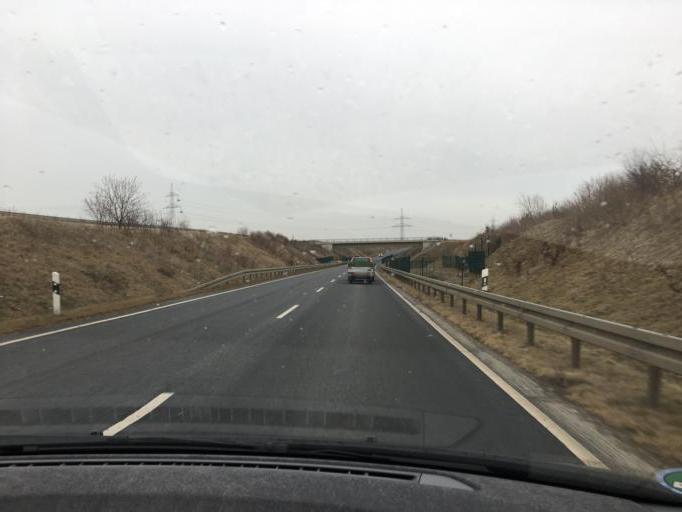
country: DE
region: North Rhine-Westphalia
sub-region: Regierungsbezirk Koln
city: Bergheim
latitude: 50.9021
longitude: 6.6261
